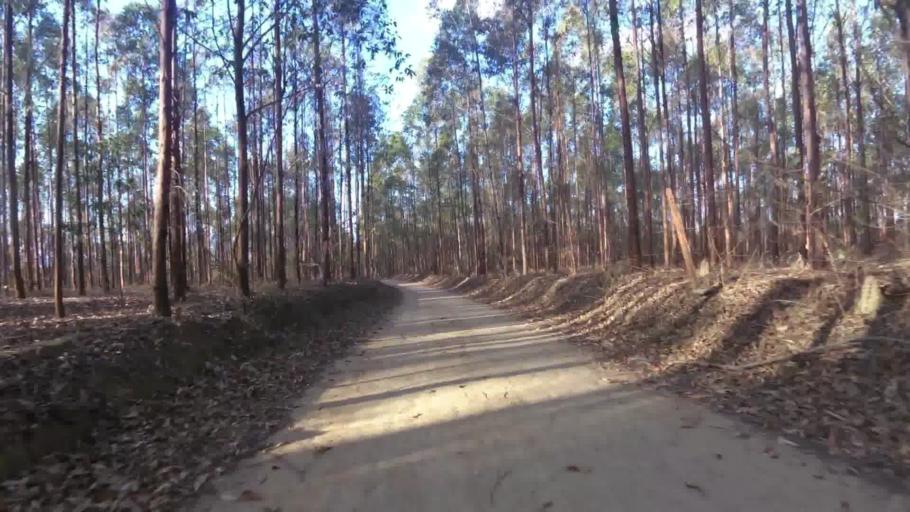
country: BR
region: Espirito Santo
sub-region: Marataizes
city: Marataizes
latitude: -21.1640
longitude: -41.0422
